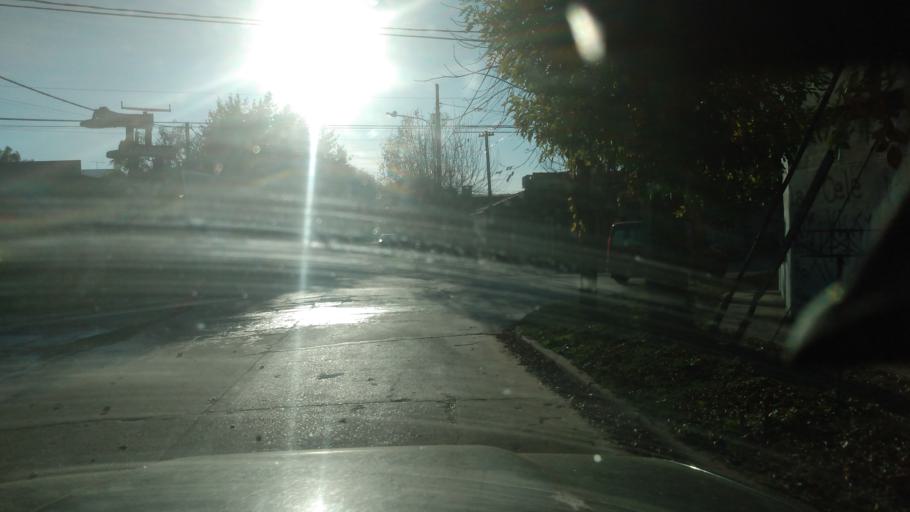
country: AR
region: Buenos Aires
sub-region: Partido de Lujan
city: Lujan
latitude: -34.5688
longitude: -59.0917
